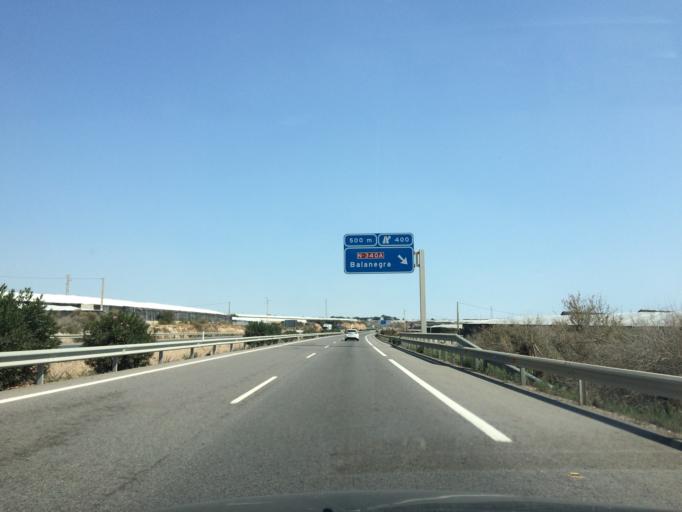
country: ES
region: Andalusia
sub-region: Provincia de Almeria
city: Dalias
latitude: 36.7556
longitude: -2.9049
